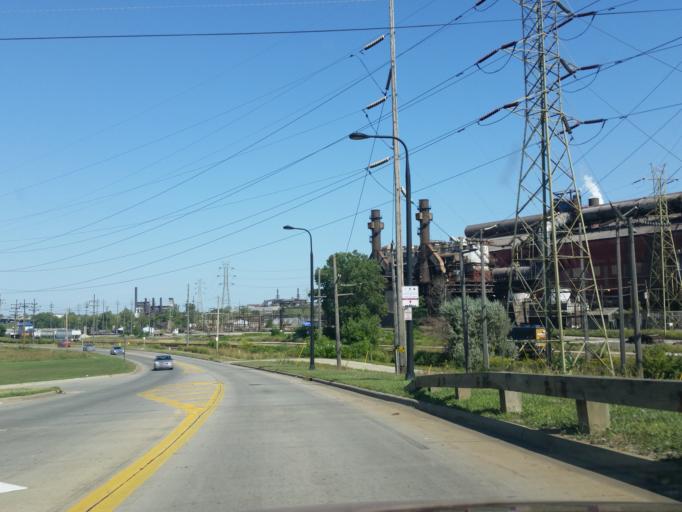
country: US
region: Ohio
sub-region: Cuyahoga County
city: Newburgh Heights
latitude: 41.4668
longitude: -81.6852
